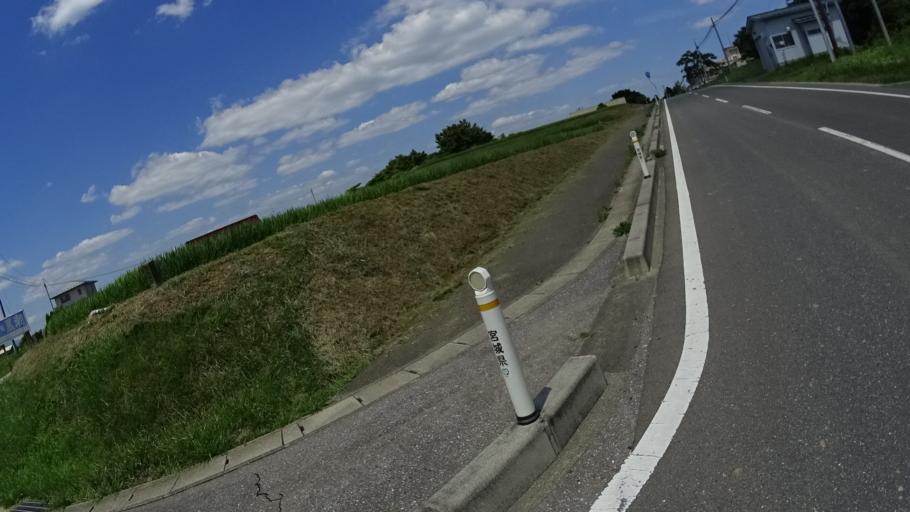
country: JP
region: Iwate
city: Ofunato
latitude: 38.8457
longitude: 141.6186
